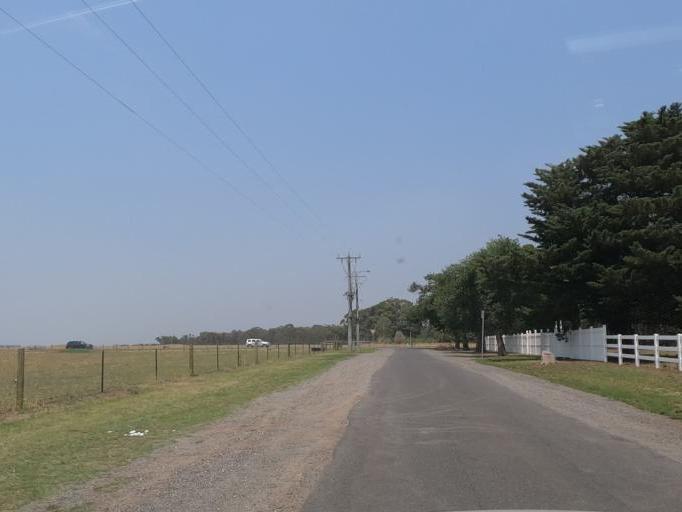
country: AU
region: Victoria
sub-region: Hume
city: Greenvale
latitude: -37.6423
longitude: 144.8291
